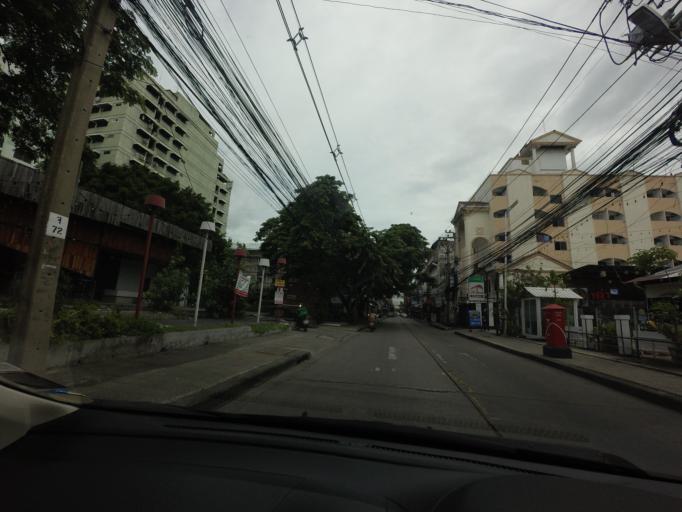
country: TH
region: Bangkok
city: Wang Thonglang
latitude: 13.7692
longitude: 100.6228
